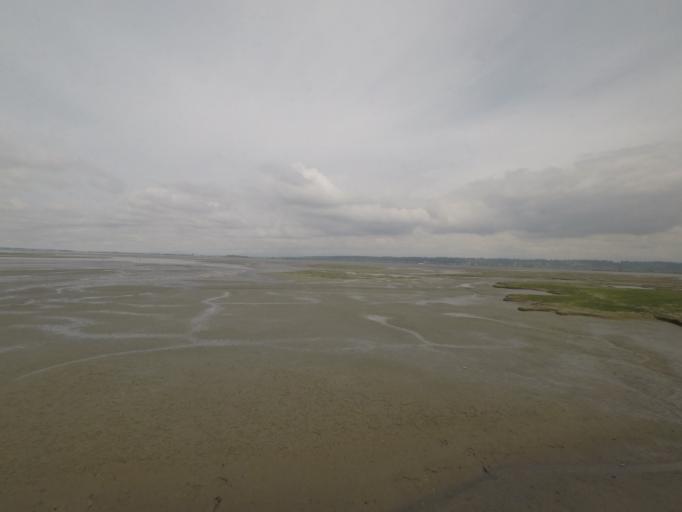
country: CA
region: British Columbia
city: Surrey
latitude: 49.0588
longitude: -122.8674
